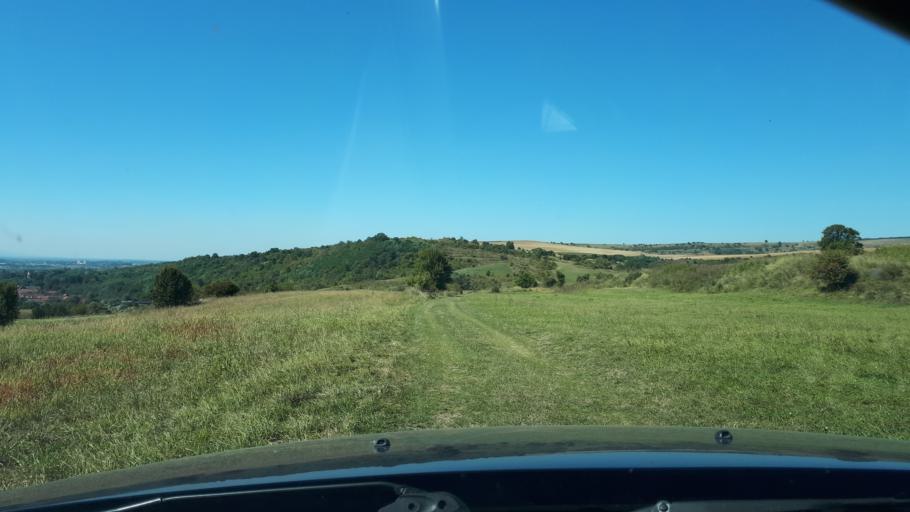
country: RO
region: Brasov
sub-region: Comuna Mandra
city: Mandra
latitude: 45.8560
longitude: 25.0644
